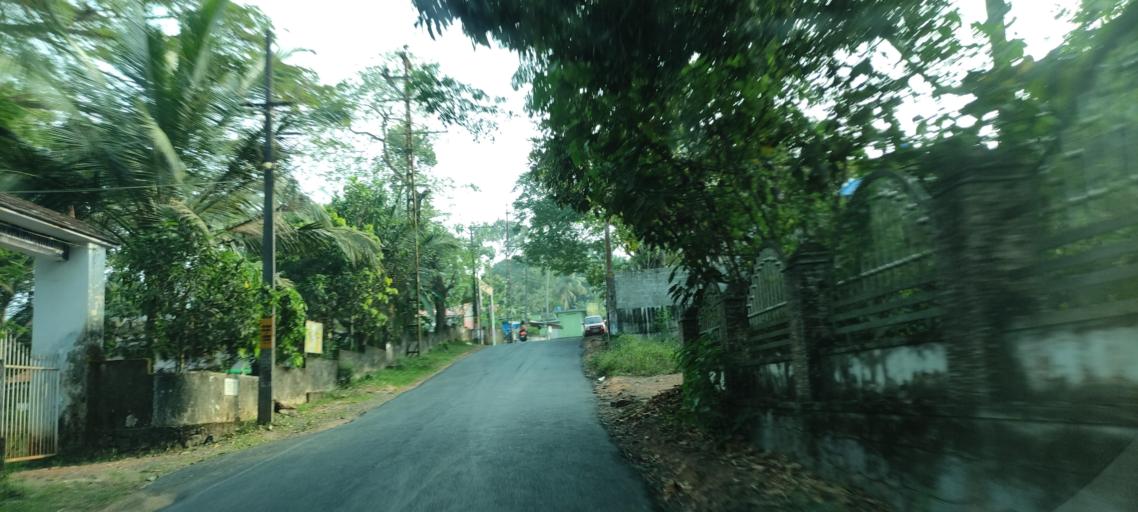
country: IN
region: Kerala
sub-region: Kottayam
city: Vaikam
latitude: 9.7231
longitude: 76.4774
